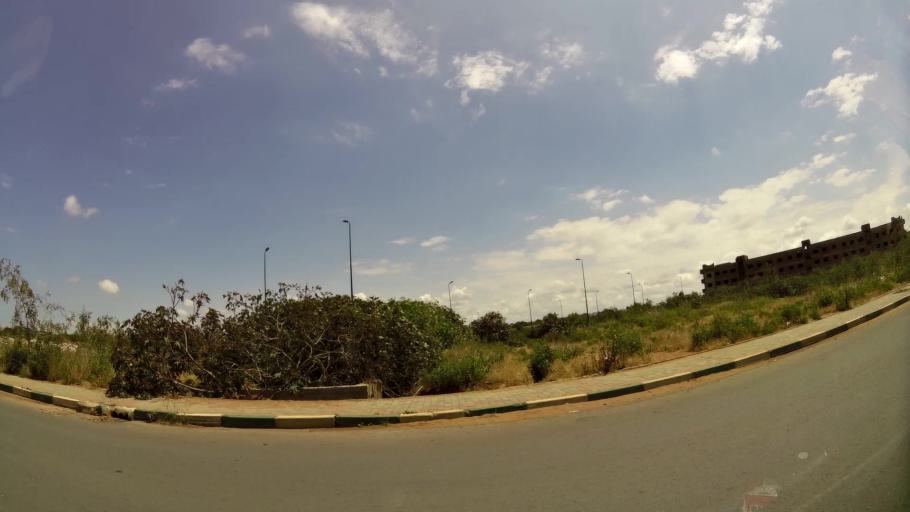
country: MA
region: Gharb-Chrarda-Beni Hssen
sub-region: Kenitra Province
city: Kenitra
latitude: 34.2585
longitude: -6.6117
